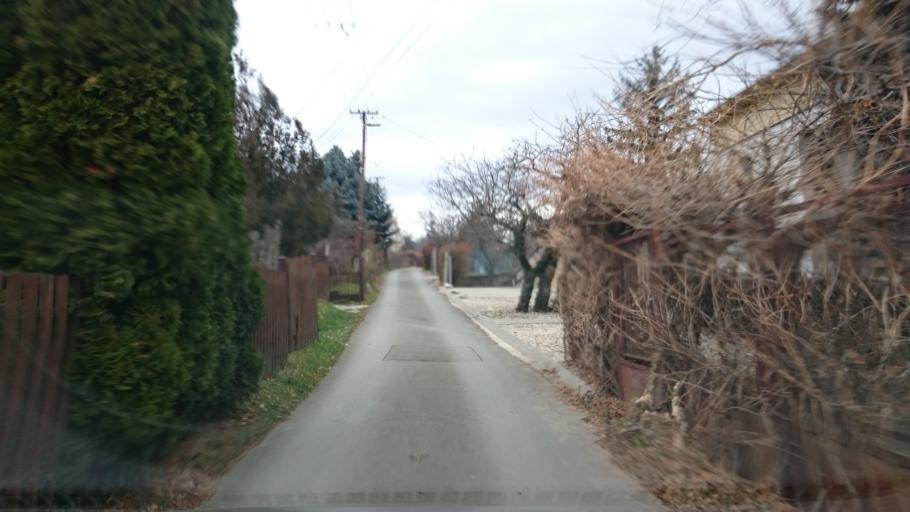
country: HU
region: Baranya
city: Pellerd
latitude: 46.0733
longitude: 18.1811
